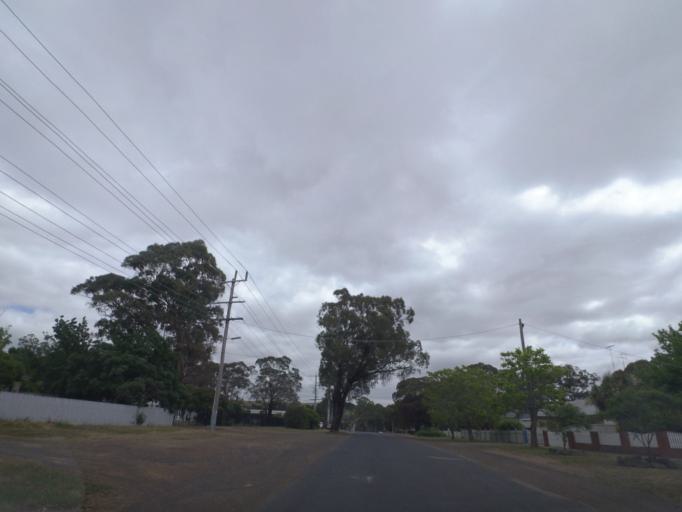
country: AU
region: Victoria
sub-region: Whittlesea
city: Whittlesea
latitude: -37.2023
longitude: 145.0425
